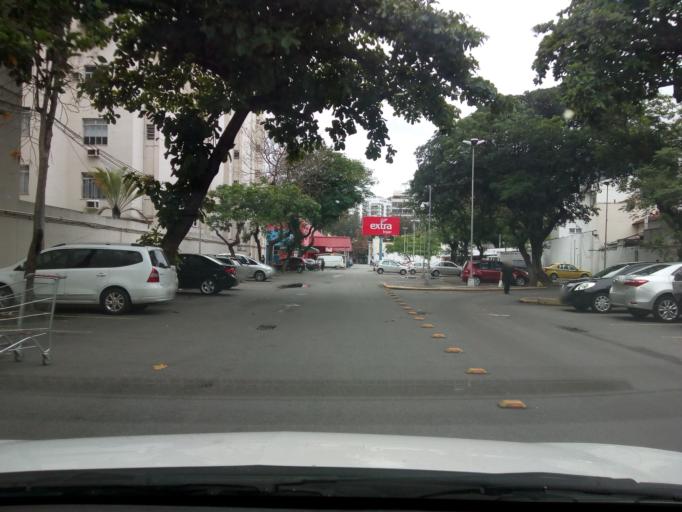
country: BR
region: Rio de Janeiro
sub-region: Rio De Janeiro
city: Rio de Janeiro
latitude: -22.9176
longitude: -43.2232
